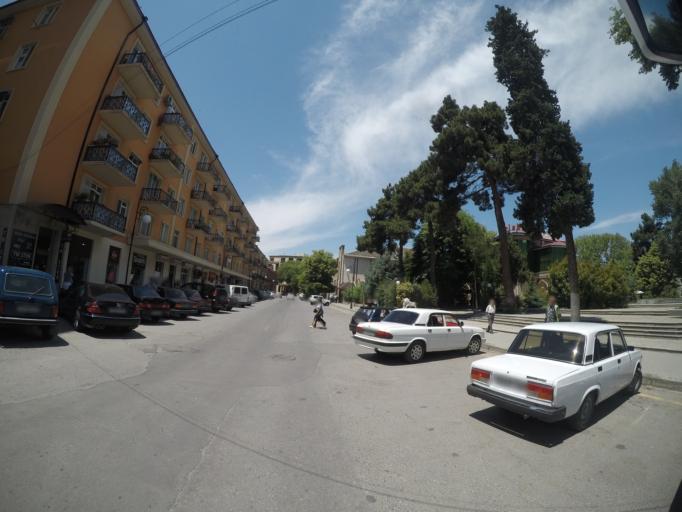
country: AZ
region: Shaki City
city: Sheki
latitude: 41.2027
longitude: 47.1801
